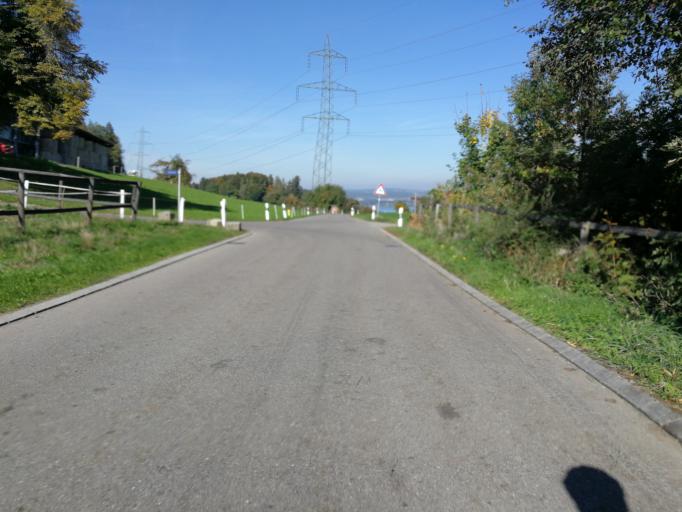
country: CH
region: Zurich
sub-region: Bezirk Uster
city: Aesch
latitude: 47.3249
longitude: 8.6676
